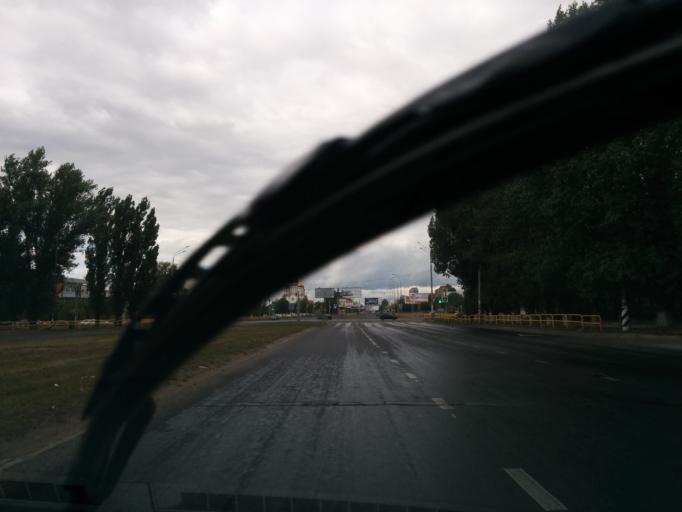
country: RU
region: Samara
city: Tol'yatti
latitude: 53.5137
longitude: 49.2781
